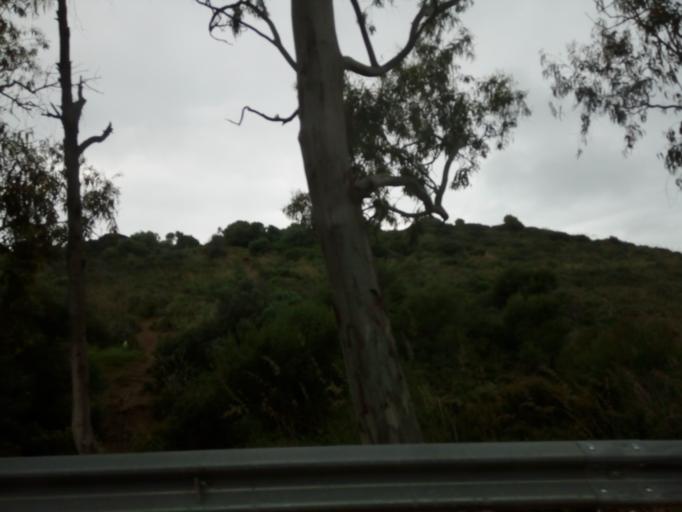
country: DZ
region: Tipaza
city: Tipasa
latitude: 36.5807
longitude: 2.5420
